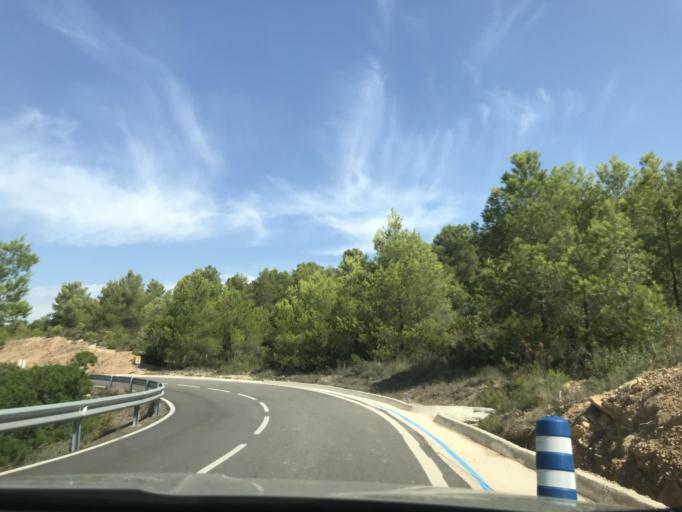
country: ES
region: Catalonia
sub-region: Provincia de Tarragona
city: Salomo
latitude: 41.2177
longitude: 1.3805
